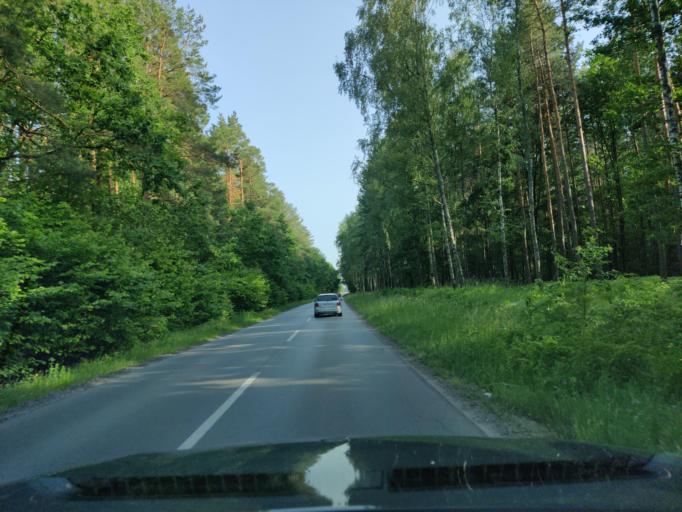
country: PL
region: Masovian Voivodeship
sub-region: Powiat wyszkowski
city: Wyszkow
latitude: 52.6258
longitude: 21.4515
